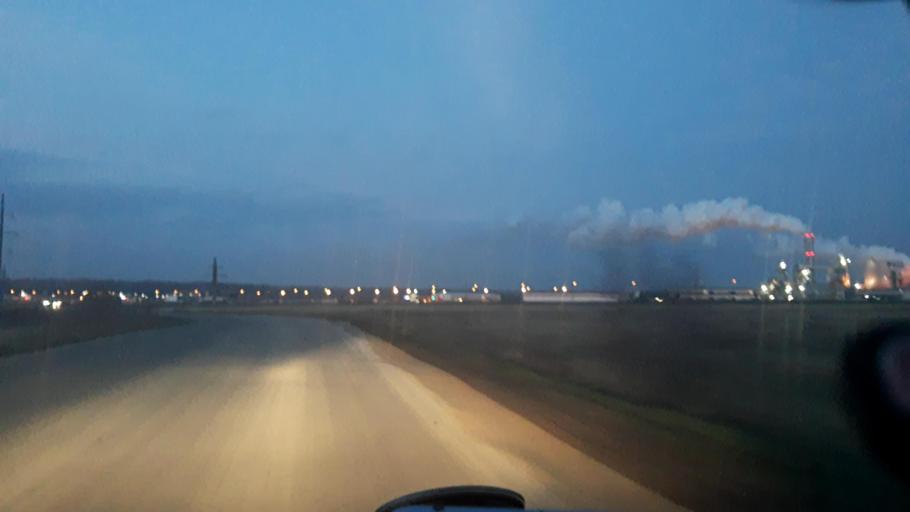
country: RU
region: Bashkortostan
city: Iglino
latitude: 54.7627
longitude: 56.2621
